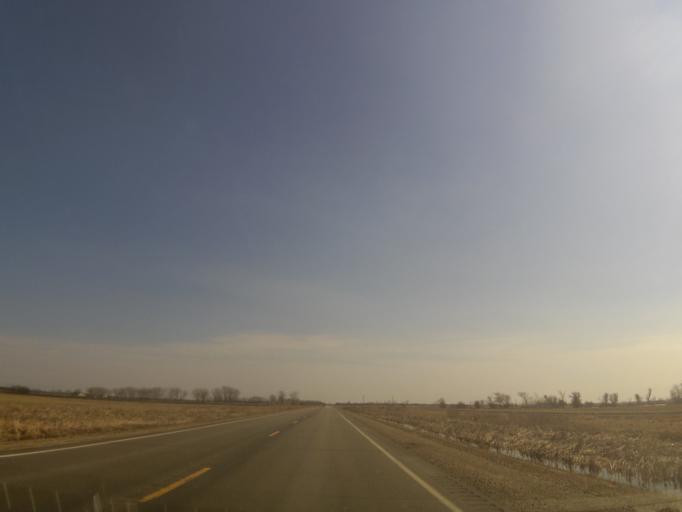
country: US
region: North Dakota
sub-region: Grand Forks County
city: Grand Forks Air Force Base
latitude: 48.1106
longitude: -97.2171
